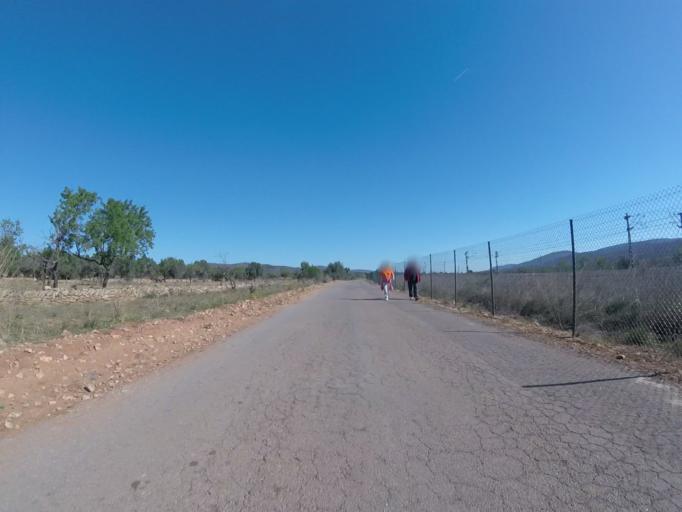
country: ES
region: Valencia
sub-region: Provincia de Castello
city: Alcala de Xivert
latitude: 40.3205
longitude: 0.2353
